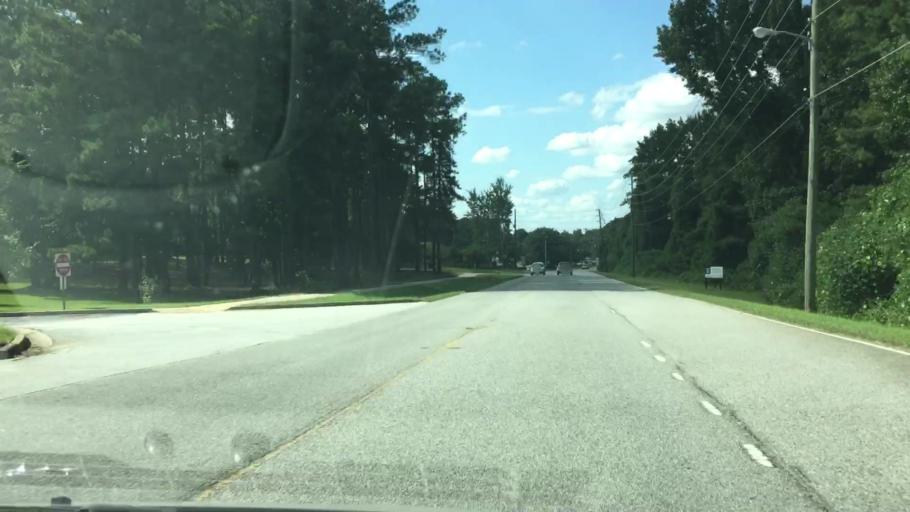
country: US
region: Georgia
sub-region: Fayette County
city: Fayetteville
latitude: 33.4436
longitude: -84.4658
